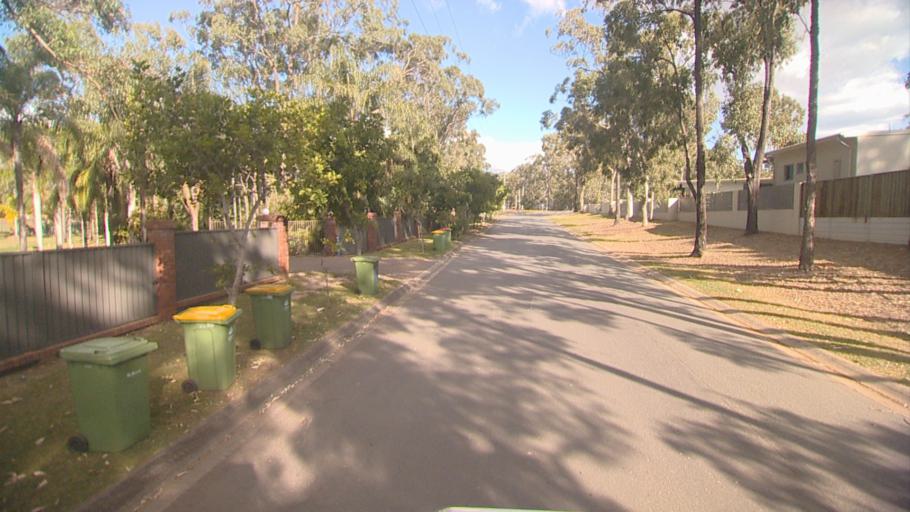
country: AU
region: Queensland
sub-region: Logan
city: Beenleigh
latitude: -27.6669
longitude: 153.2217
